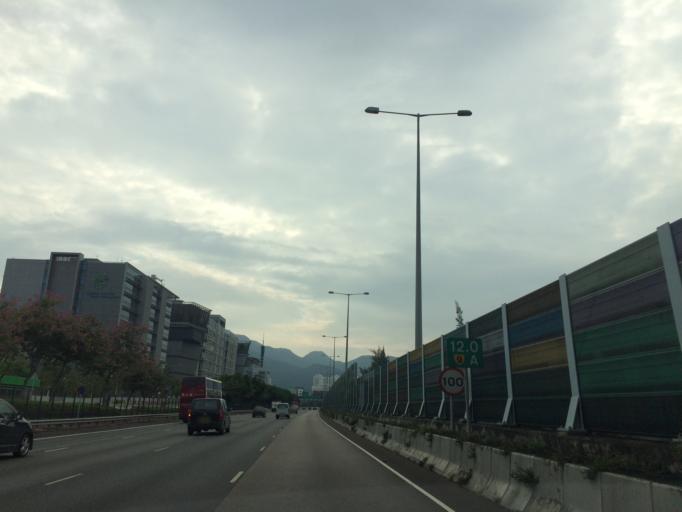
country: HK
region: Tai Po
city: Tai Po
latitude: 22.4269
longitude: 114.2070
